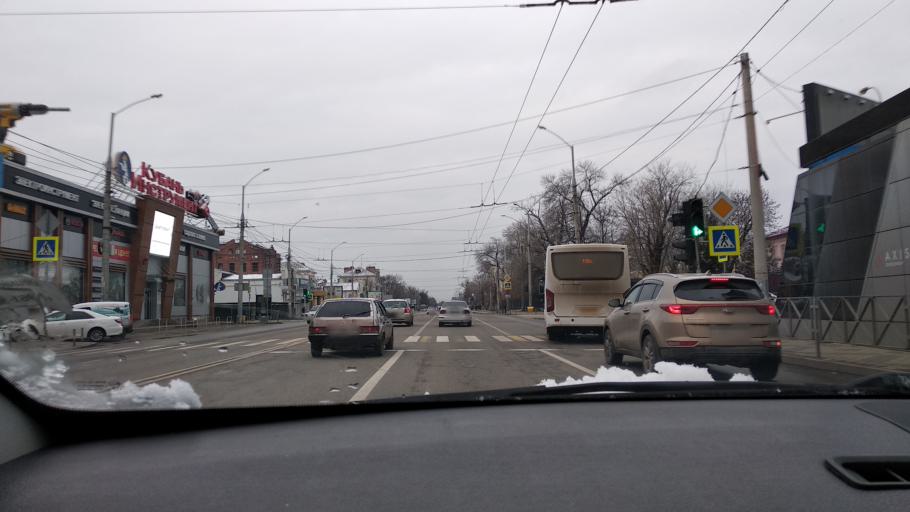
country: RU
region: Krasnodarskiy
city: Krasnodar
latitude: 45.0413
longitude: 38.9680
